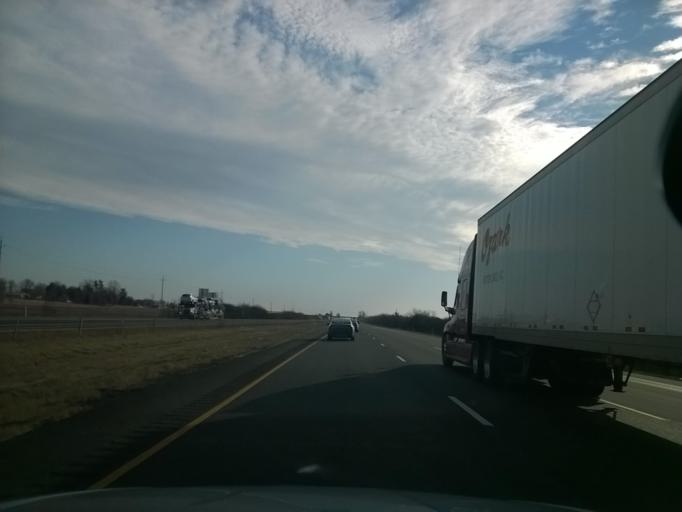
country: US
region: Indiana
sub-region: Johnson County
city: Edinburgh
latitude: 39.3575
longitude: -85.9425
